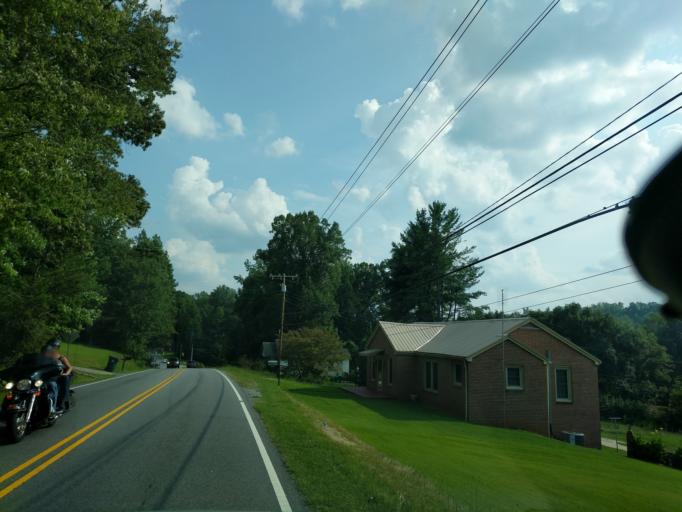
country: US
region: North Carolina
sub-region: Rutherford County
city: Rutherfordton
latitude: 35.3424
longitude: -81.9634
